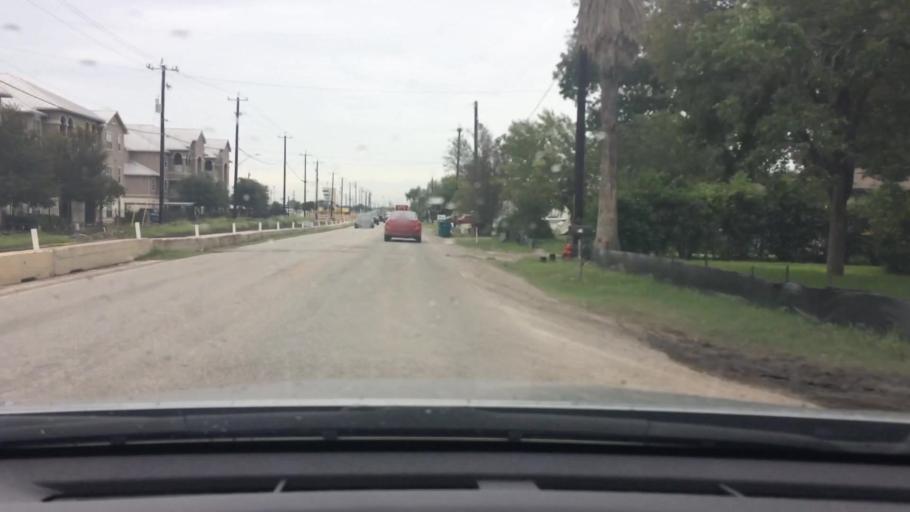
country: US
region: Texas
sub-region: Bexar County
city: Converse
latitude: 29.5146
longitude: -98.3117
